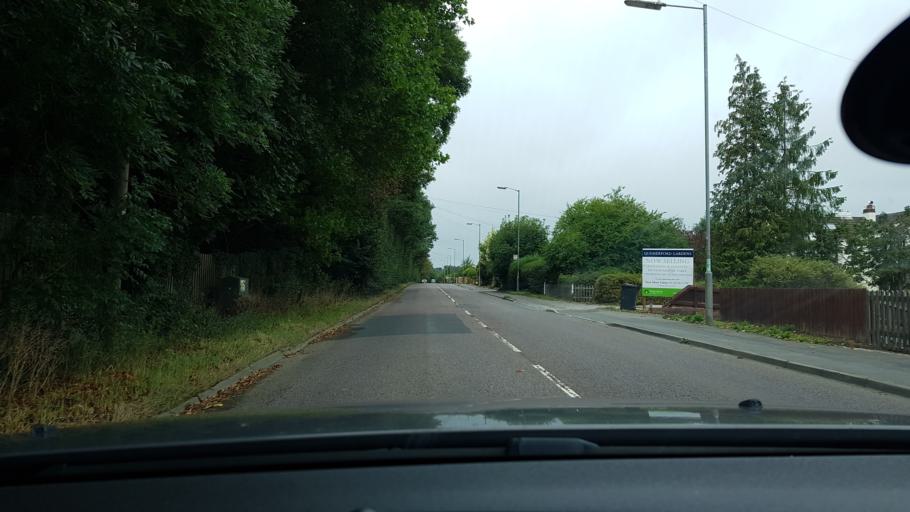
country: GB
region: England
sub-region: Wiltshire
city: Calne
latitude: 51.4262
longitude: -1.9826
